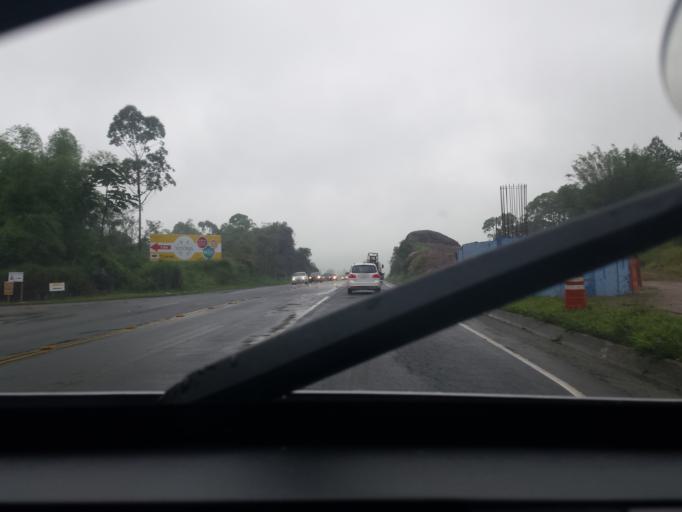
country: BR
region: Santa Catarina
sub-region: Itajai
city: Itajai
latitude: -26.8337
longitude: -48.7381
